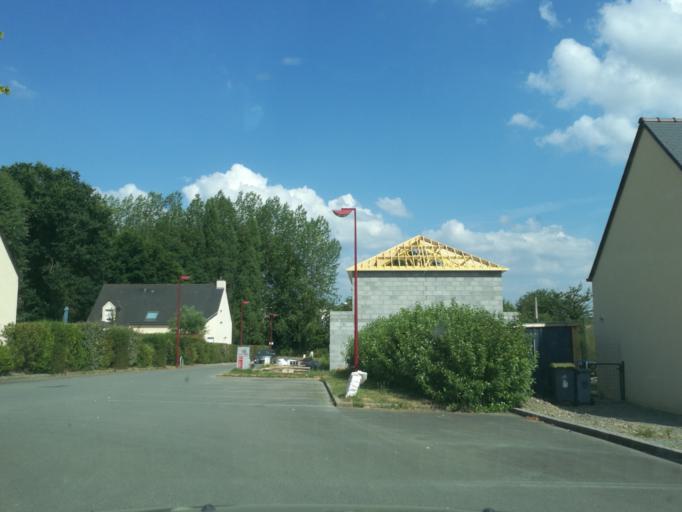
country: FR
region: Brittany
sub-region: Departement d'Ille-et-Vilaine
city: Montauban-de-Bretagne
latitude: 48.1937
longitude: -2.0409
